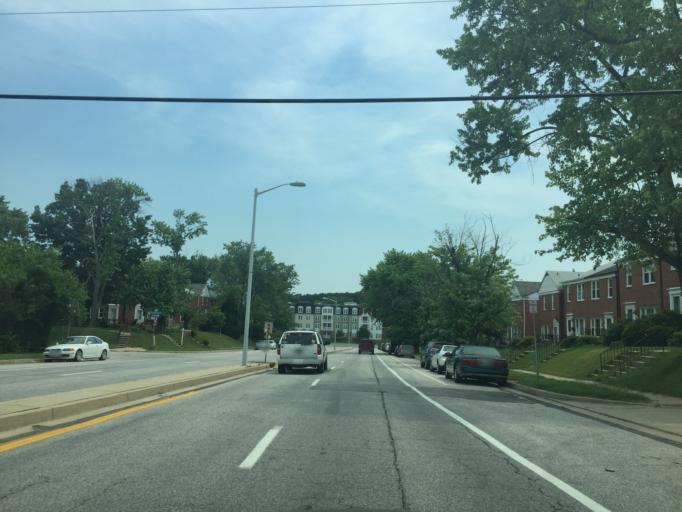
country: US
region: Maryland
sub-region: Baltimore County
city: Towson
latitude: 39.4072
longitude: -76.6062
